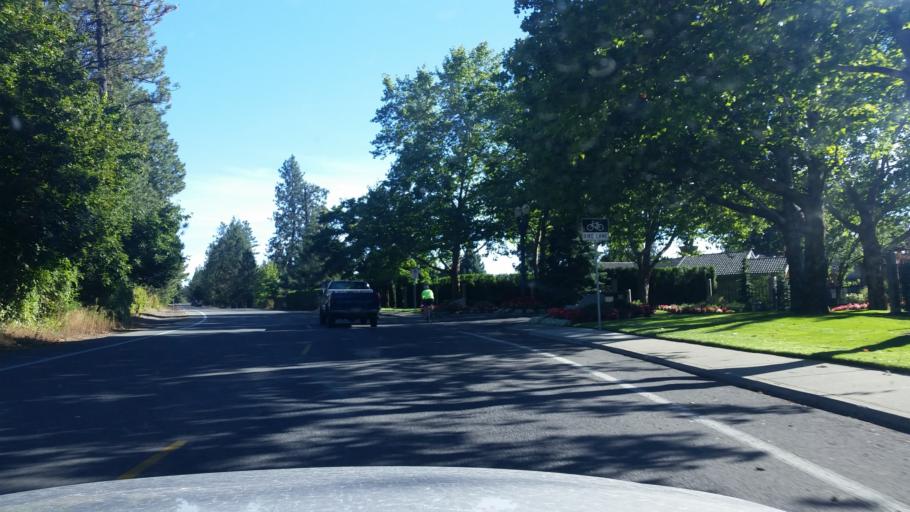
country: US
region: Washington
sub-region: Spokane County
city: Spokane
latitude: 47.6137
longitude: -117.3992
